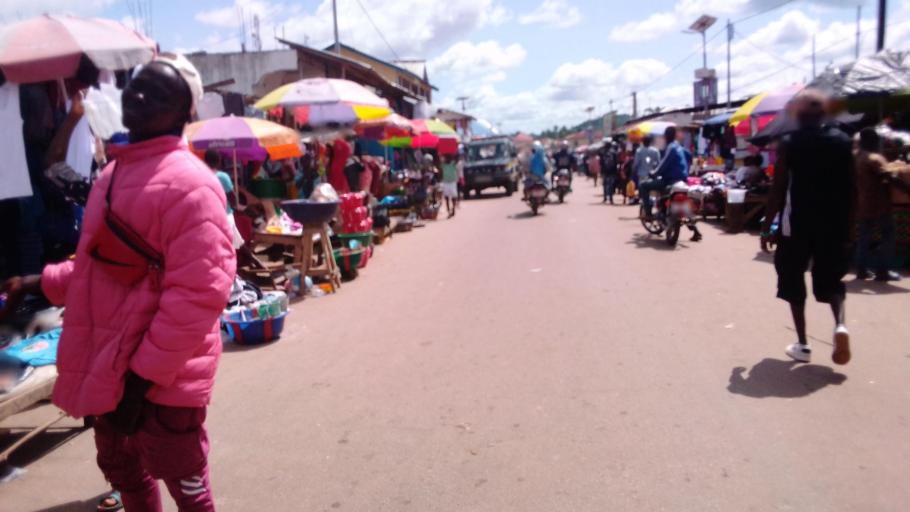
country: SL
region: Northern Province
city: Makeni
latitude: 8.8880
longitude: -12.0421
